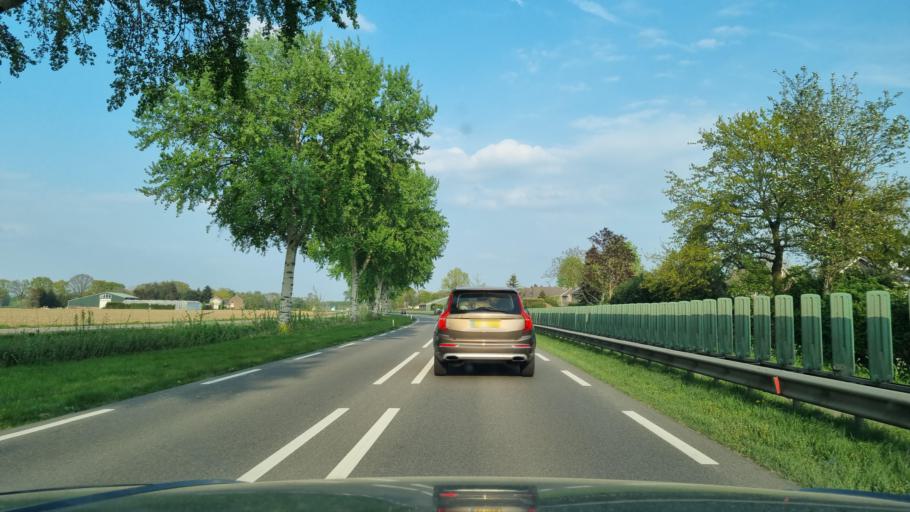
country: NL
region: North Brabant
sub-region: Gemeente Cuijk
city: Cuijk
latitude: 51.7267
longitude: 5.8319
